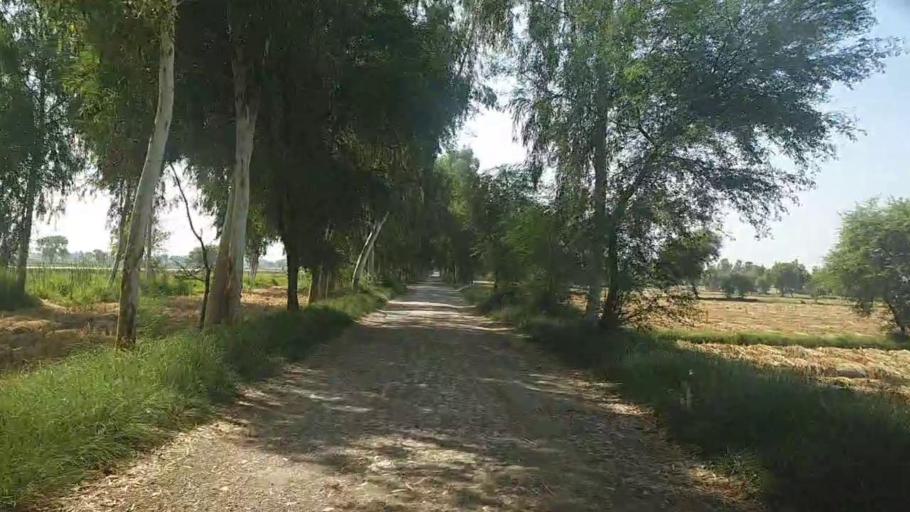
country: PK
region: Sindh
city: Thul
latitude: 28.2409
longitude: 68.7958
